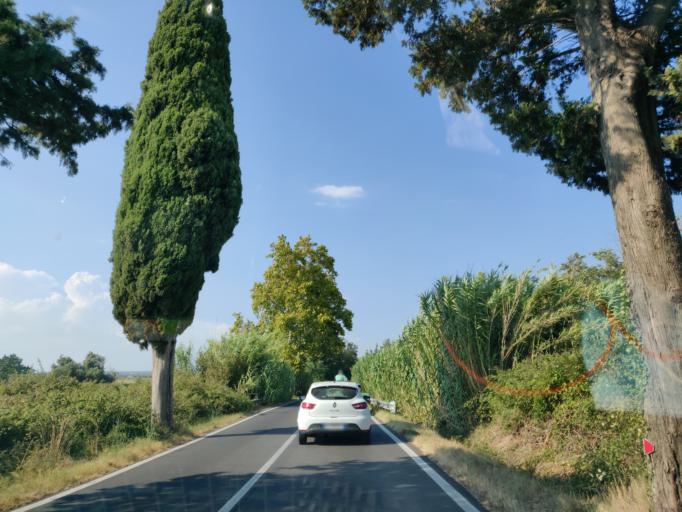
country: IT
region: Latium
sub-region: Provincia di Viterbo
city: Canino
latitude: 42.4062
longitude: 11.6952
